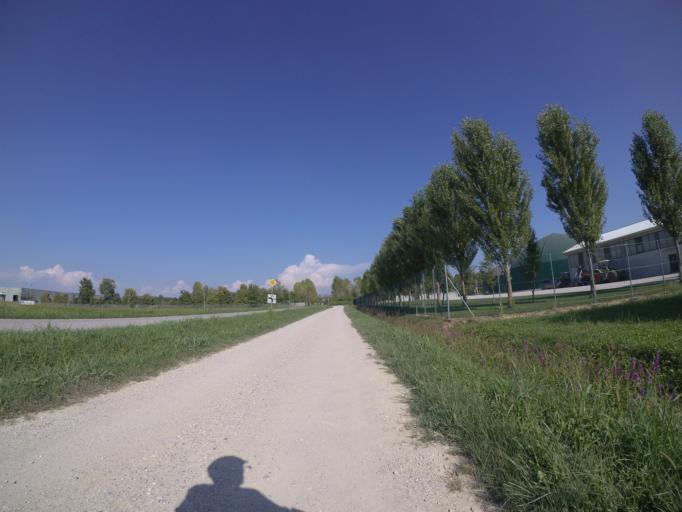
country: IT
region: Friuli Venezia Giulia
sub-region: Provincia di Udine
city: Pocenia
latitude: 45.8303
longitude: 13.1135
